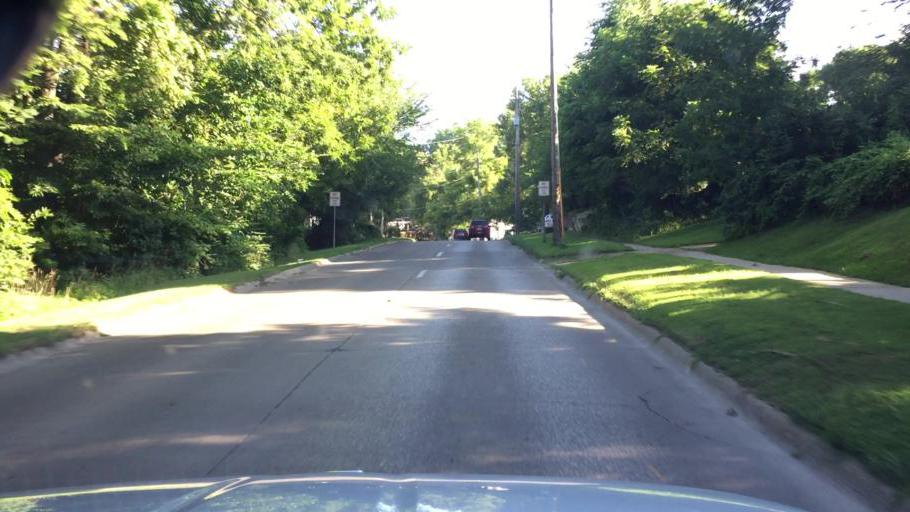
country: US
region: Iowa
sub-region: Johnson County
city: Iowa City
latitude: 41.6708
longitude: -91.5227
